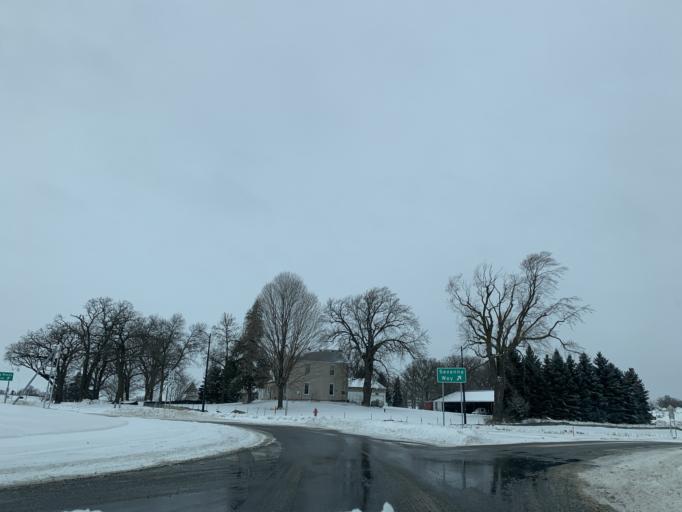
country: US
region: Minnesota
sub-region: Carver County
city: Chaska
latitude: 44.7911
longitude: -93.6250
